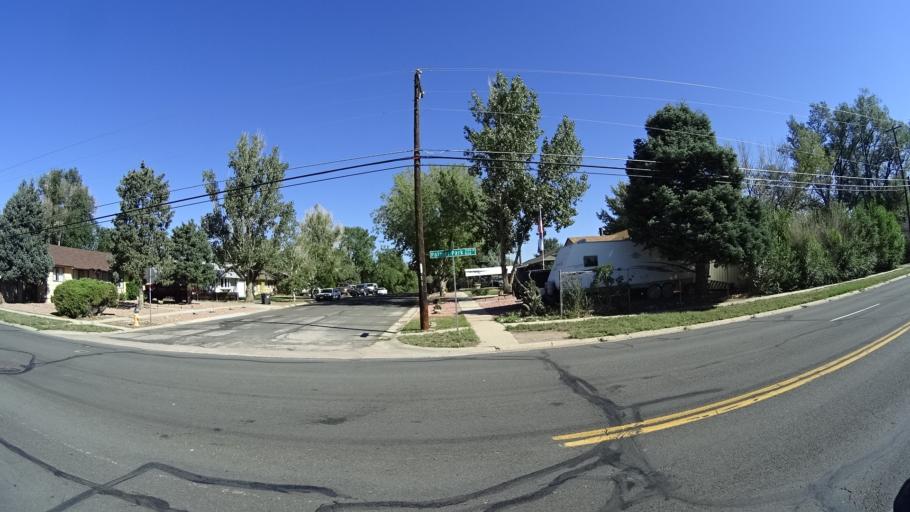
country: US
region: Colorado
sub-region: El Paso County
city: Colorado Springs
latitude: 38.8544
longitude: -104.7675
